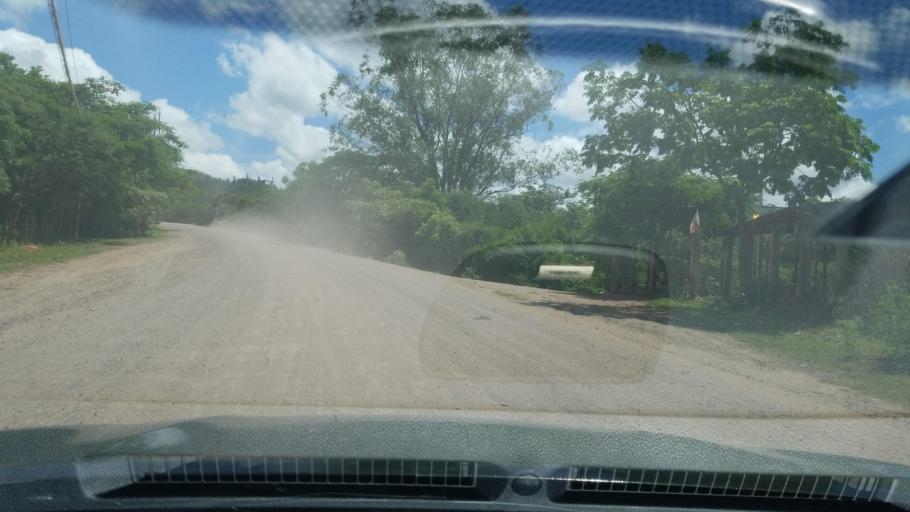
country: HN
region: Francisco Morazan
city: San Juan de Flores
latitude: 14.3302
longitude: -87.0460
